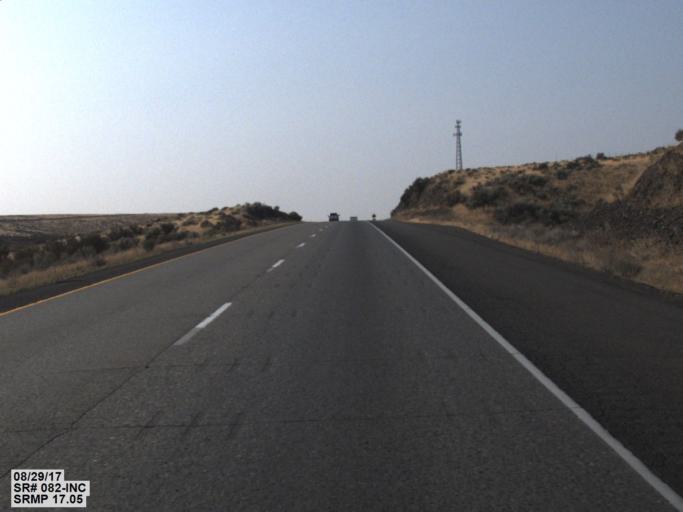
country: US
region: Washington
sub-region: Yakima County
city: Terrace Heights
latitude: 46.7757
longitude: -120.3756
